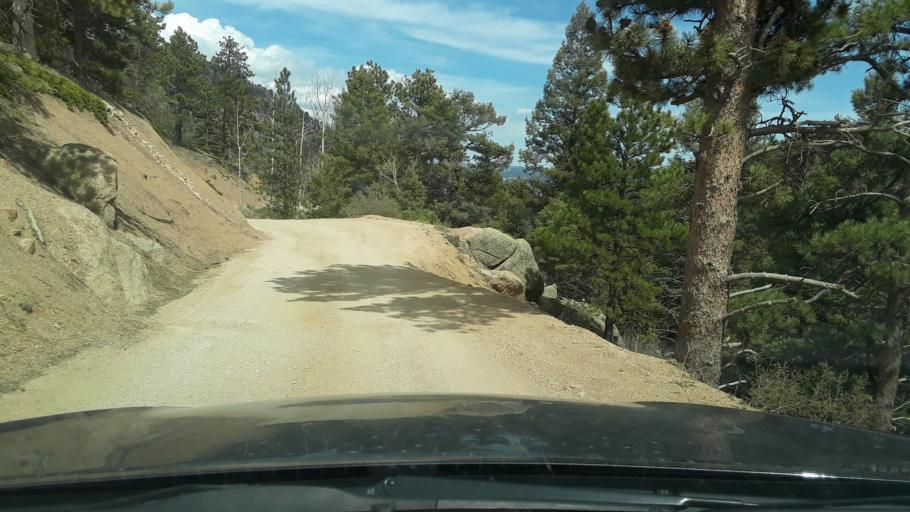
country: US
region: Colorado
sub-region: El Paso County
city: Palmer Lake
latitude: 39.0670
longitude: -104.9395
